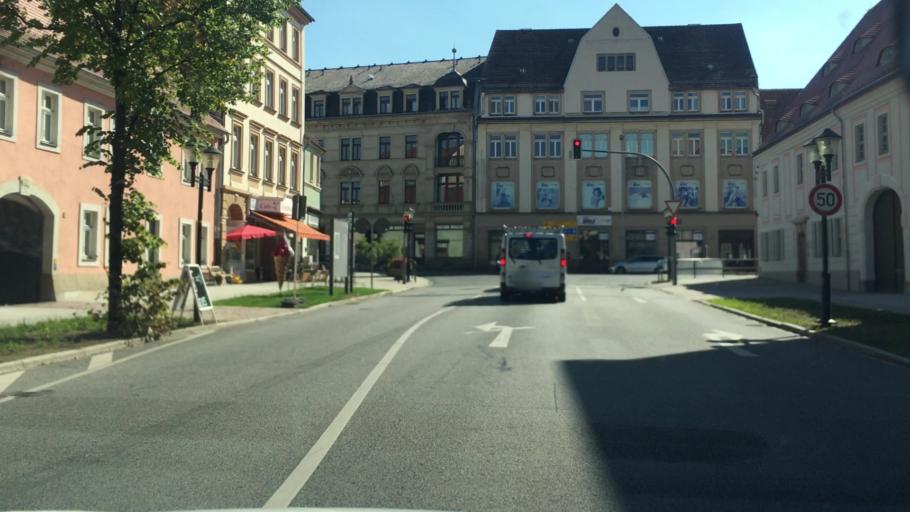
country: DE
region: Saxony
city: Pirna
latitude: 50.9585
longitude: 13.9390
